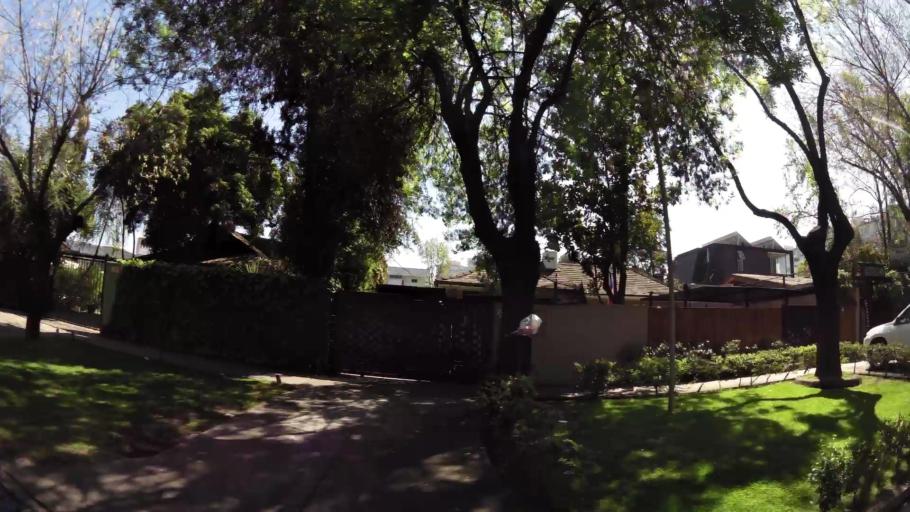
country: CL
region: Santiago Metropolitan
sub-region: Provincia de Santiago
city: Villa Presidente Frei, Nunoa, Santiago, Chile
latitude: -33.4107
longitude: -70.5453
